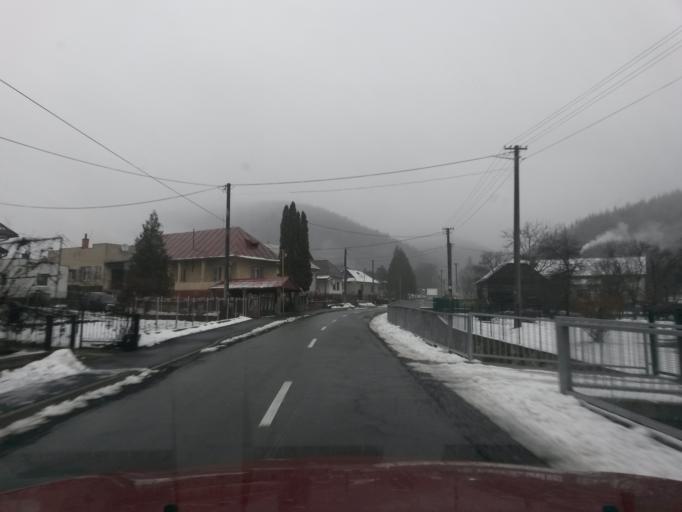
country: SK
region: Presovsky
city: Humenne
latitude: 49.0928
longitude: 21.8255
